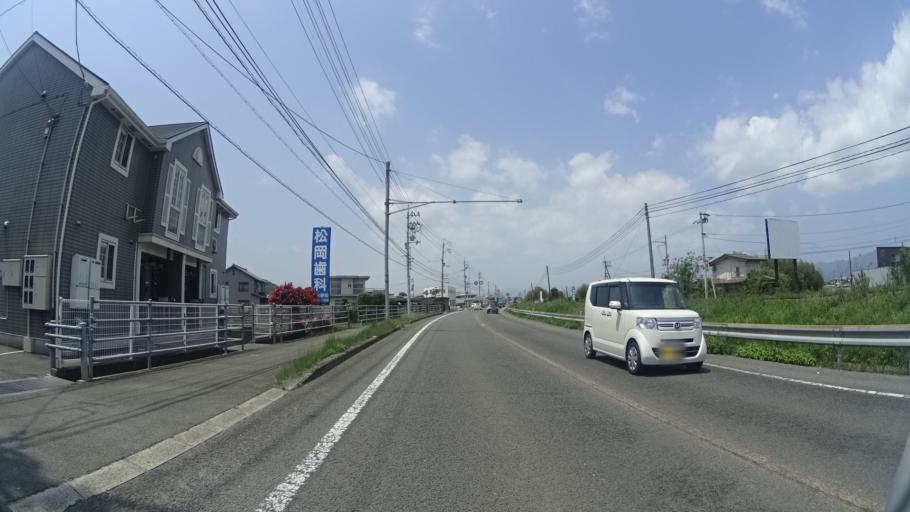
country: JP
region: Tokushima
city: Ishii
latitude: 34.0653
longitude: 134.4315
